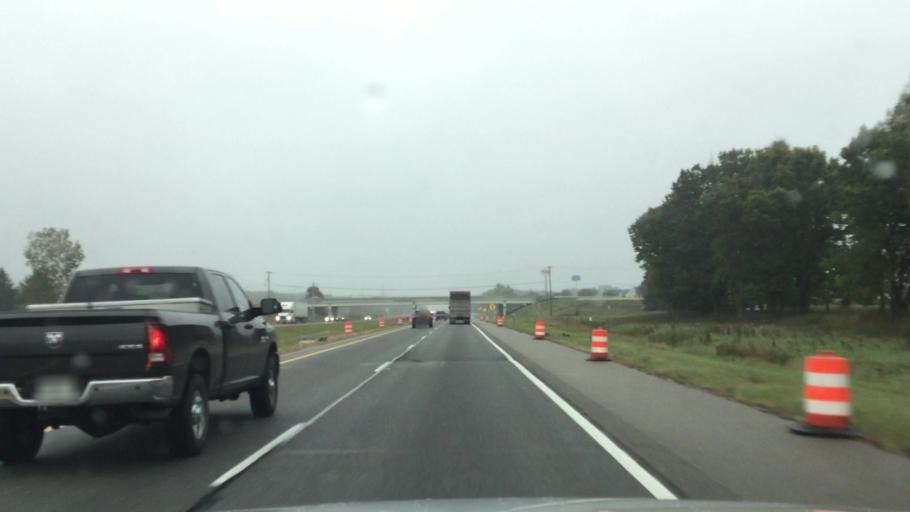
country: US
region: Michigan
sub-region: Kalamazoo County
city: Westwood
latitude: 42.2376
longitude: -85.6817
